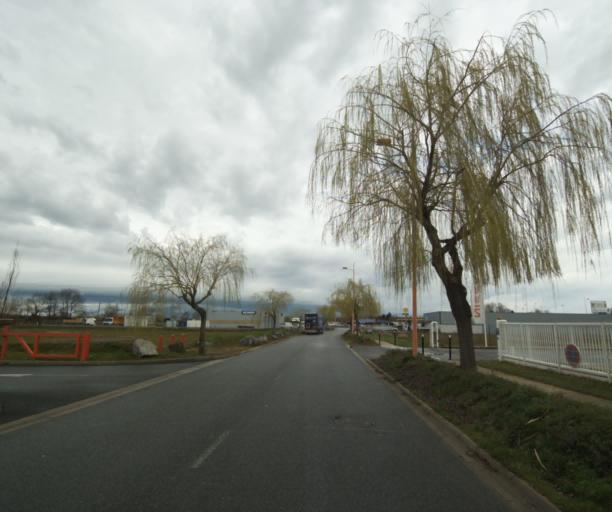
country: FR
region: Auvergne
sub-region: Departement de l'Allier
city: Toulon-sur-Allier
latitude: 46.5039
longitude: 3.3616
